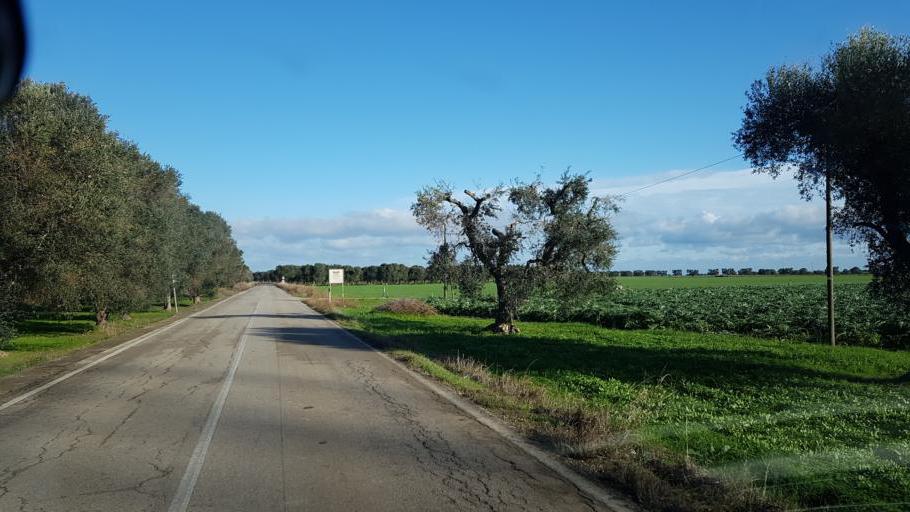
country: IT
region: Apulia
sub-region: Provincia di Brindisi
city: Tuturano
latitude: 40.5606
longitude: 17.9481
